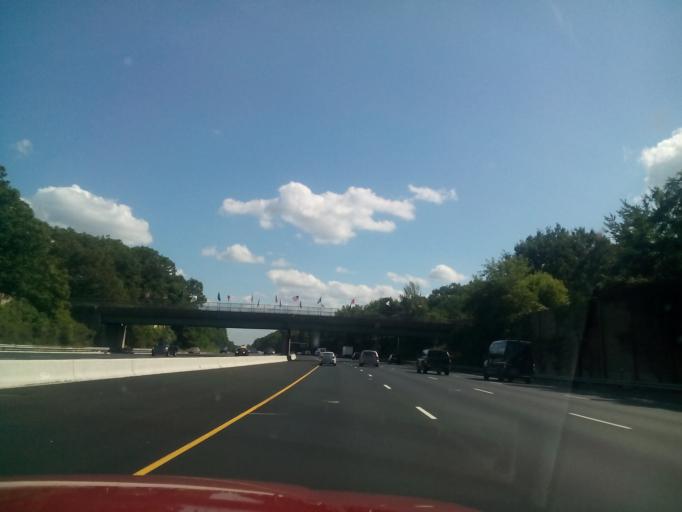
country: US
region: New Jersey
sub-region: Morris County
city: Mountain Lakes
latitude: 40.8787
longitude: -74.4687
